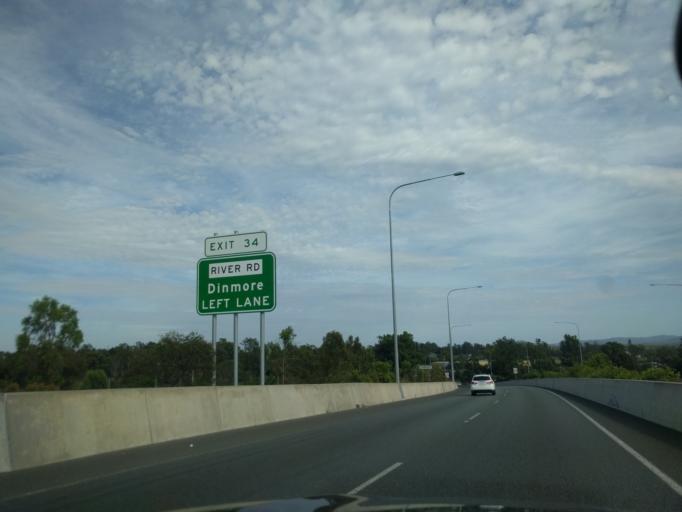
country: AU
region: Queensland
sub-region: Ipswich
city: Riverview
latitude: -27.5946
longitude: 152.8402
